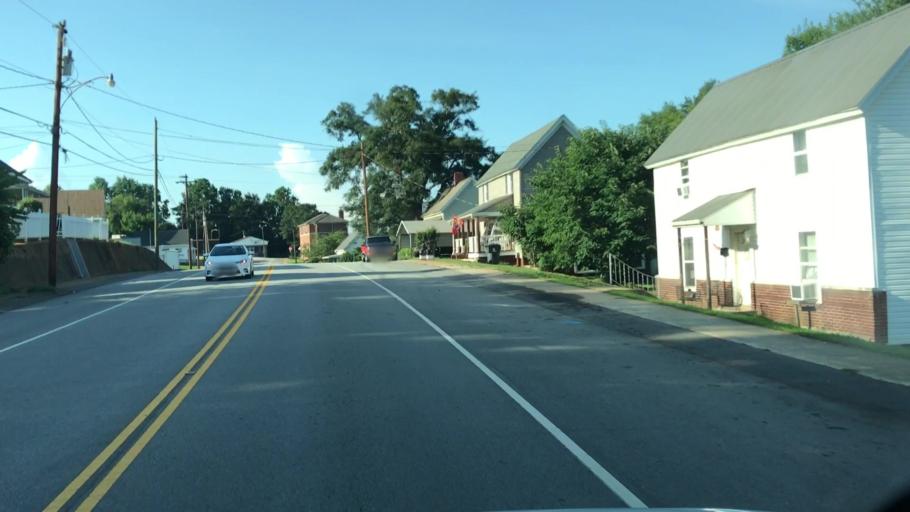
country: US
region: South Carolina
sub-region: Anderson County
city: Williamston
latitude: 34.6399
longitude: -82.4570
